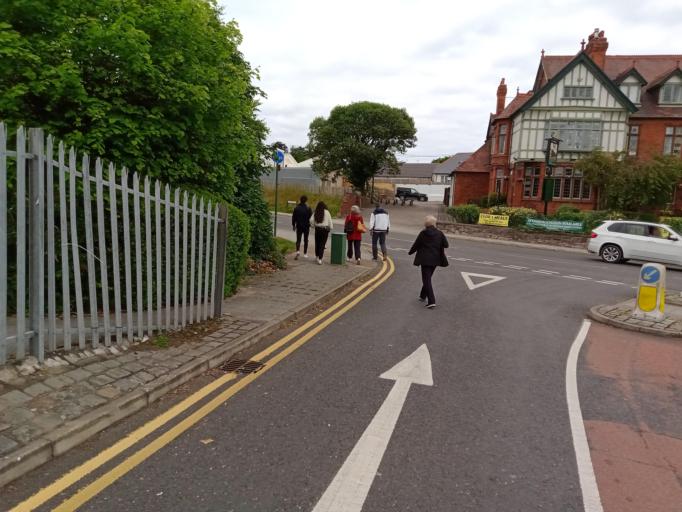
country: GB
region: Wales
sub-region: Conwy
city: Llansantffraid Glan Conwy
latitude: 53.2846
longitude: -3.8101
